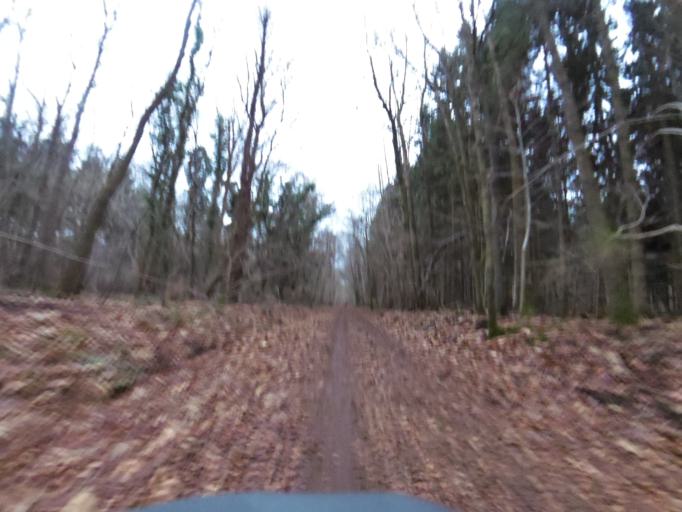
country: GB
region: England
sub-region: Norfolk
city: Costessey
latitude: 52.7063
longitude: 1.1832
